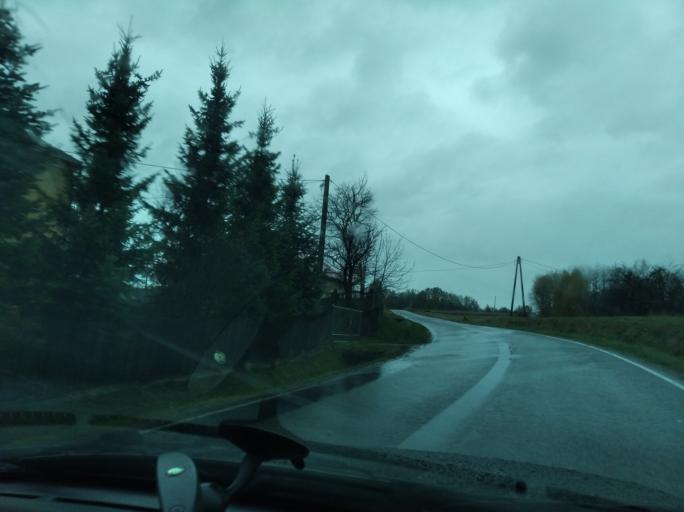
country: PL
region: Subcarpathian Voivodeship
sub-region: Powiat lancucki
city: Handzlowka
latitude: 49.9822
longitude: 22.1925
